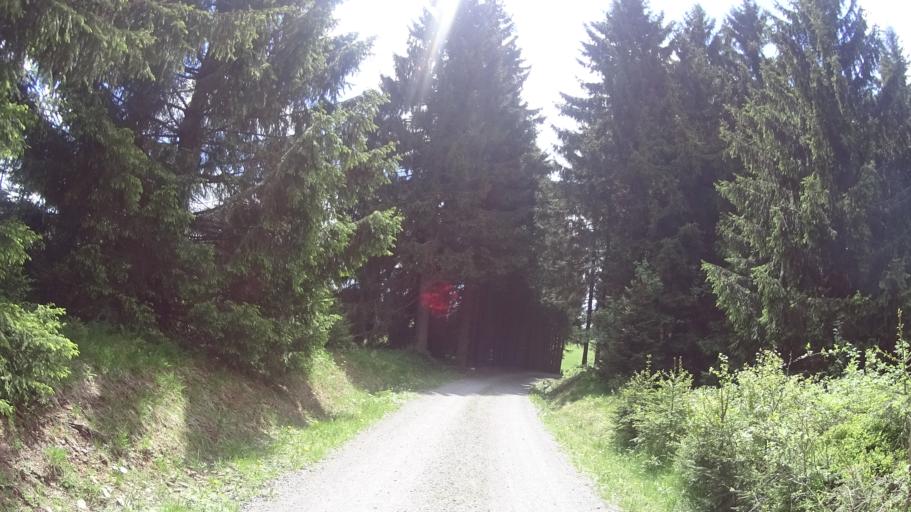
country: DE
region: Thuringia
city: Neustadt am Rennsteig
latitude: 50.5903
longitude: 10.9186
